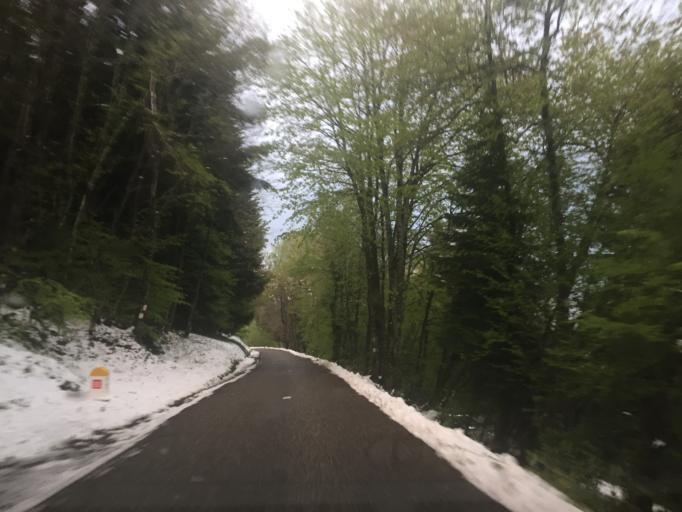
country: FR
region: Rhone-Alpes
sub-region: Departement de la Savoie
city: La Motte-Servolex
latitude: 45.5876
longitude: 5.8281
